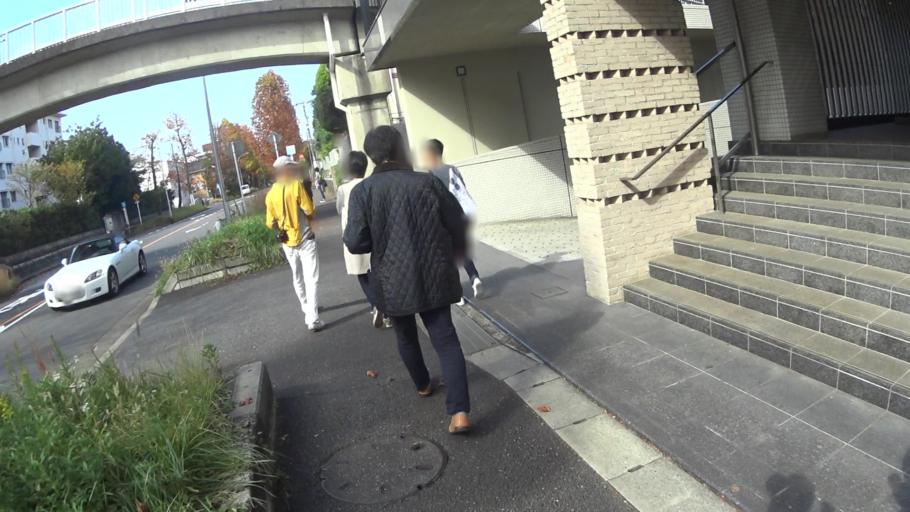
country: JP
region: Tokyo
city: Chofugaoka
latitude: 35.5833
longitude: 139.5556
